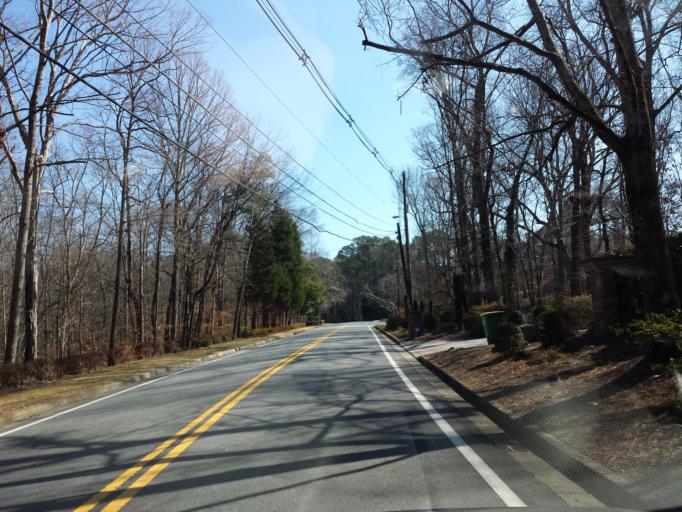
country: US
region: Georgia
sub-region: Fulton County
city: Sandy Springs
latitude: 33.9177
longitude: -84.4286
